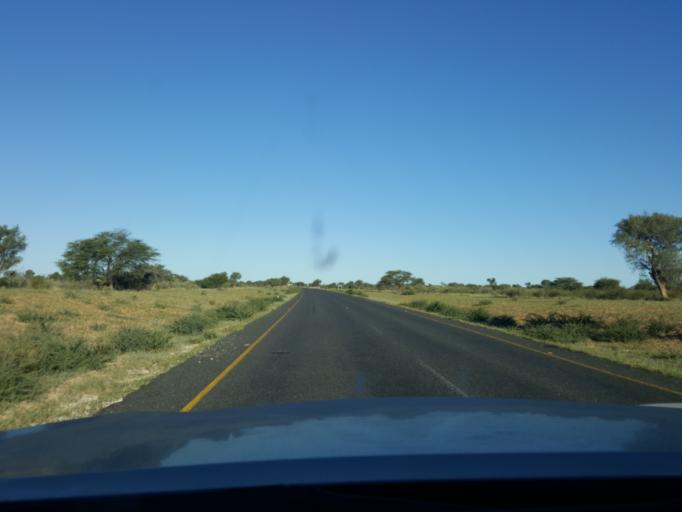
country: BW
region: Southern
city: Khakhea
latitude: -24.2264
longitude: 23.2400
